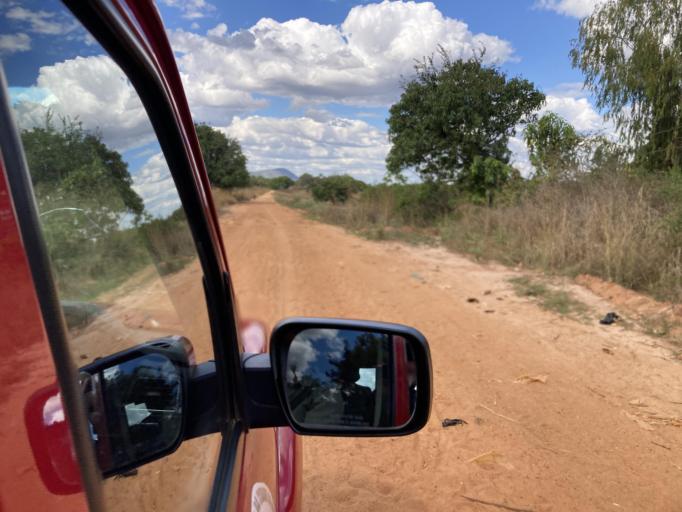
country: MZ
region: Cabo Delgado
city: Montepuez
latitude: -13.1264
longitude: 39.0385
